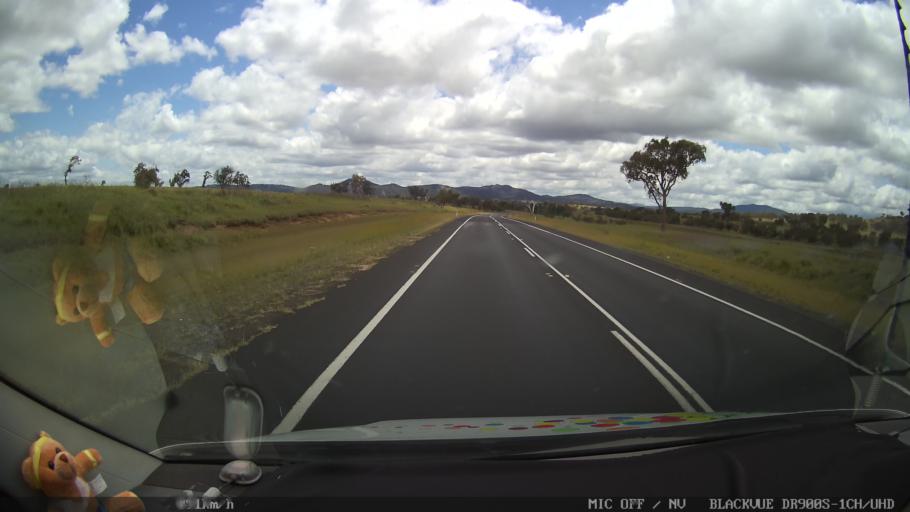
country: AU
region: New South Wales
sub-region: Glen Innes Severn
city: Glen Innes
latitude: -29.3940
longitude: 151.8802
